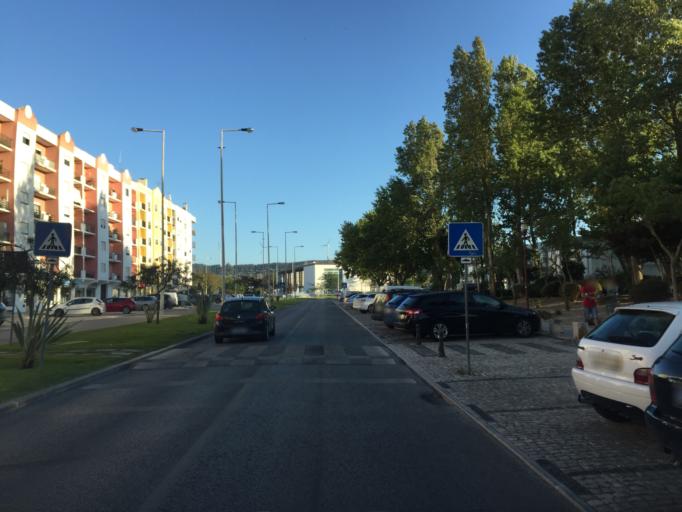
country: PT
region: Lisbon
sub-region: Torres Vedras
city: Torres Vedras
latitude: 39.0856
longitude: -9.2612
